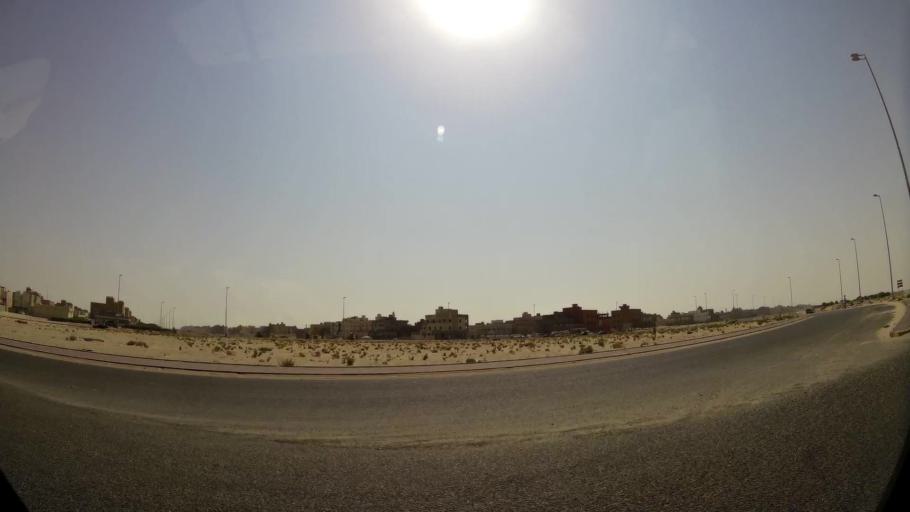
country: KW
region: Al Ahmadi
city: Al Wafrah
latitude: 28.8047
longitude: 48.0441
